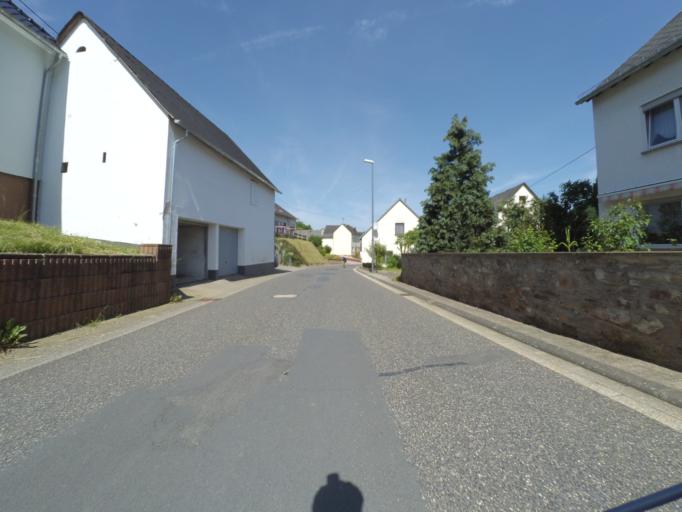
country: DE
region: Rheinland-Pfalz
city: Kalenborn
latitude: 50.2598
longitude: 7.0791
